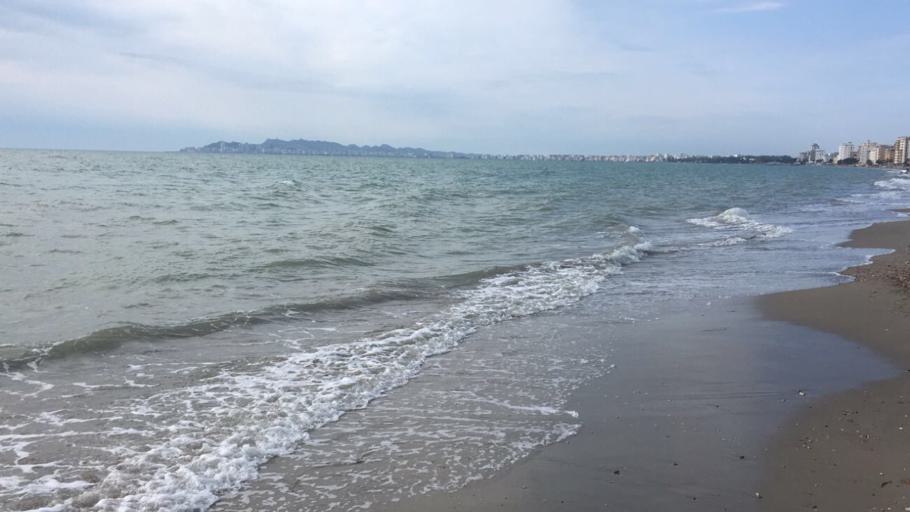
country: AL
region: Tirane
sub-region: Rrethi i Kavajes
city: Golem
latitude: 41.2612
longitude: 19.5191
